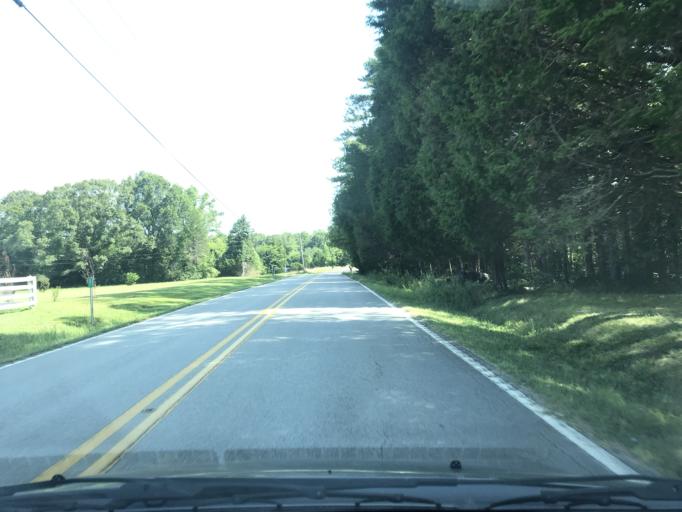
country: US
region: Tennessee
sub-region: Hamilton County
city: Sale Creek
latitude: 35.3428
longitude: -85.0029
